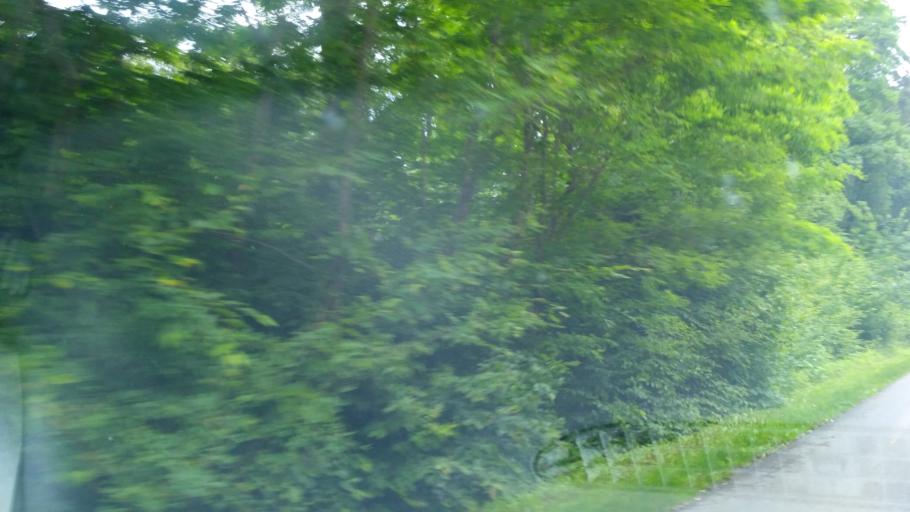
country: PL
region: Subcarpathian Voivodeship
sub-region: Powiat jaroslawski
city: Pruchnik
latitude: 49.8913
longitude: 22.5252
